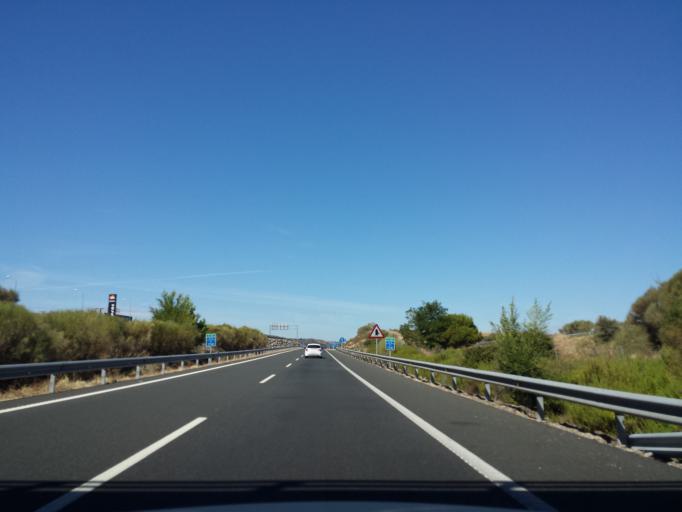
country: ES
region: Extremadura
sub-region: Provincia de Caceres
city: Peraleda de la Mata
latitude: 39.8895
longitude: -5.4668
